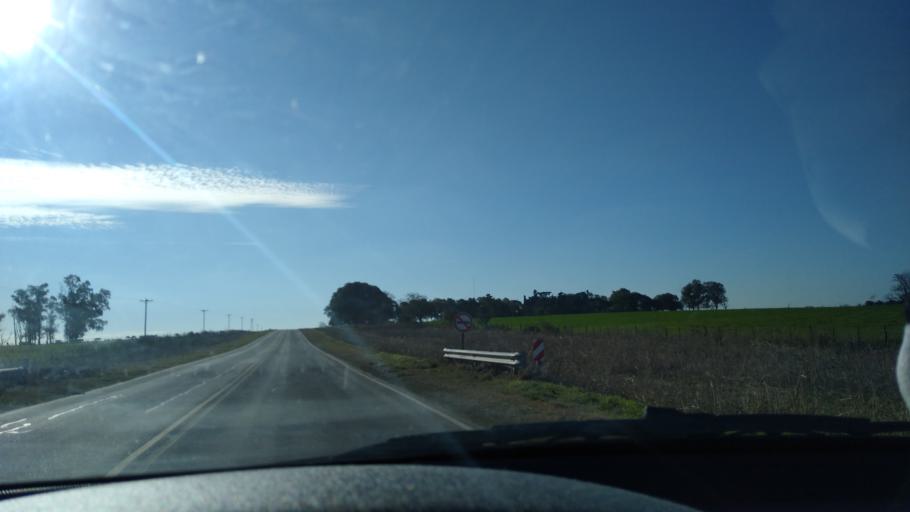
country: AR
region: Entre Rios
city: Aranguren
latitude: -32.3920
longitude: -60.3310
